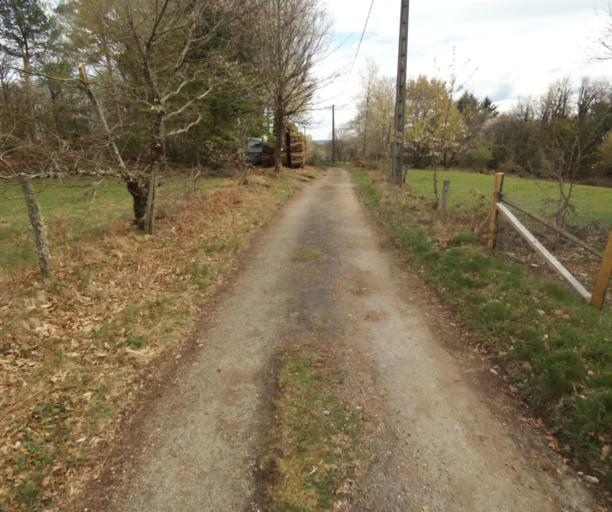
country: FR
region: Limousin
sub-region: Departement de la Correze
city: Argentat
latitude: 45.1812
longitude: 1.9372
